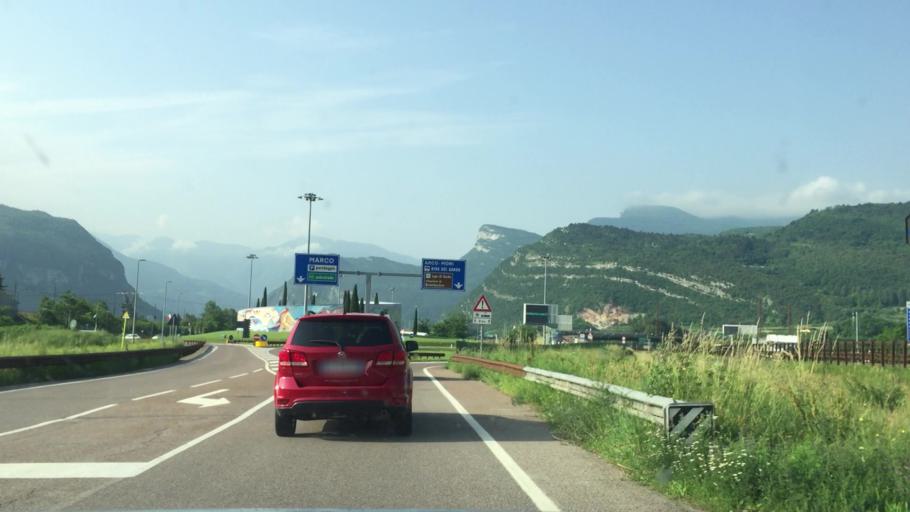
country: IT
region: Trentino-Alto Adige
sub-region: Provincia di Trento
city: Marco
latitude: 45.8523
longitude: 11.0016
